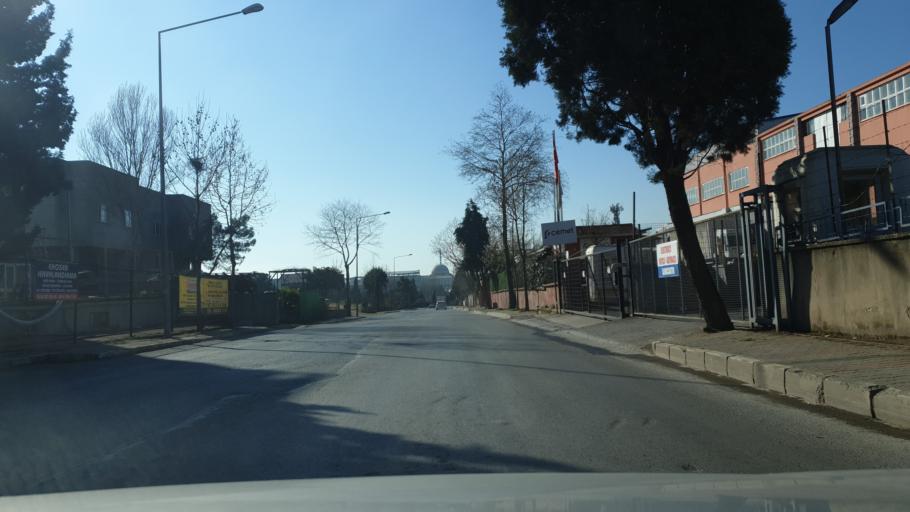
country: TR
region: Istanbul
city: Icmeler
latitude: 40.8782
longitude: 29.3619
